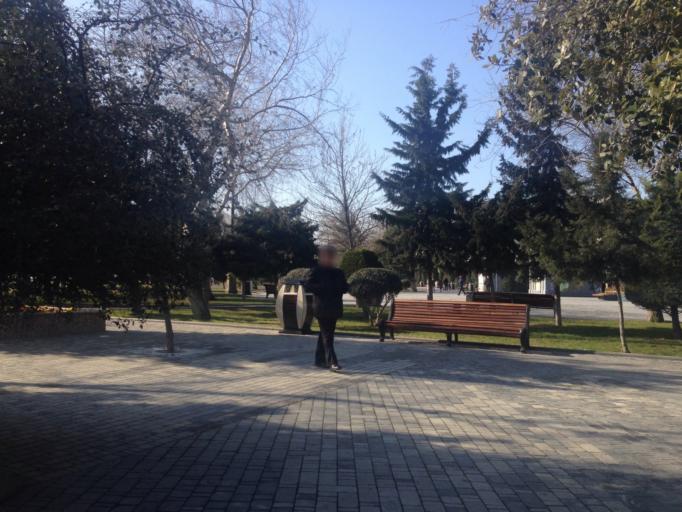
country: AZ
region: Baki
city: Baku
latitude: 40.3711
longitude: 49.8527
